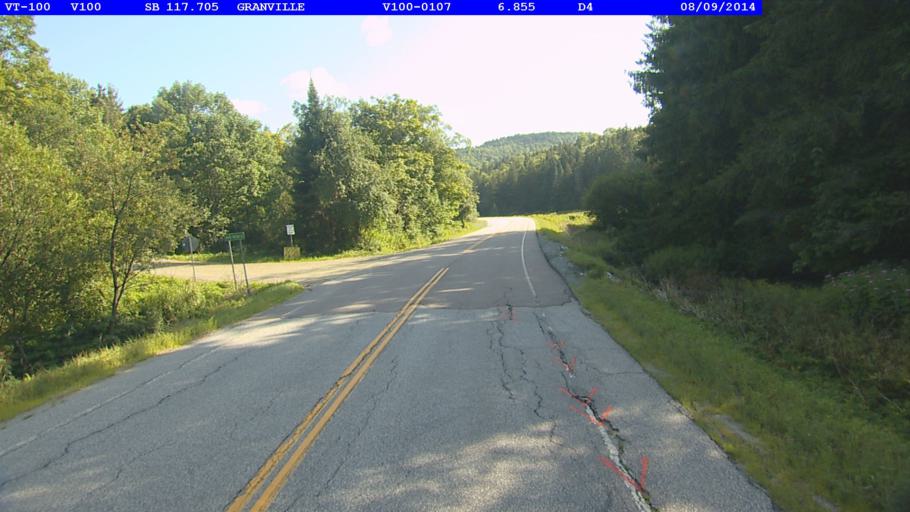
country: US
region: Vermont
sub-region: Orange County
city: Randolph
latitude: 44.0292
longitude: -72.8336
